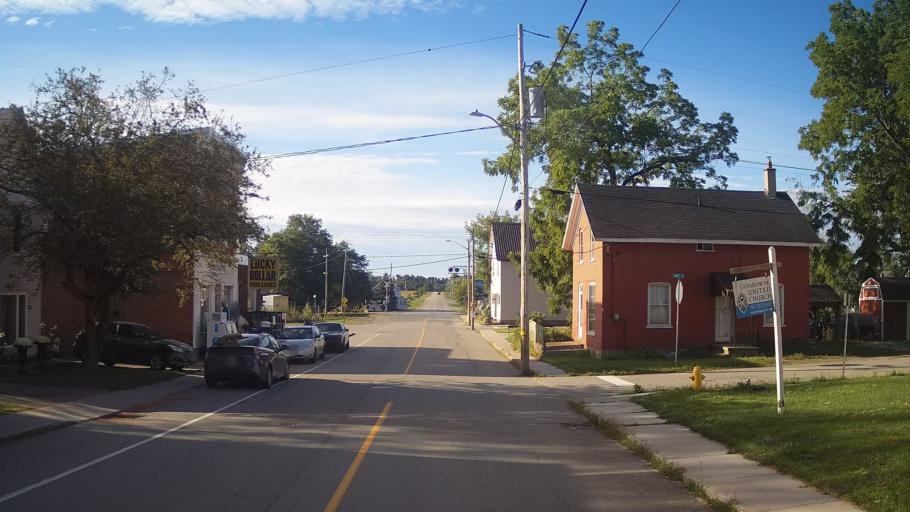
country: US
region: New York
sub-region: Jefferson County
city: Alexandria Bay
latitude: 44.4042
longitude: -76.0181
